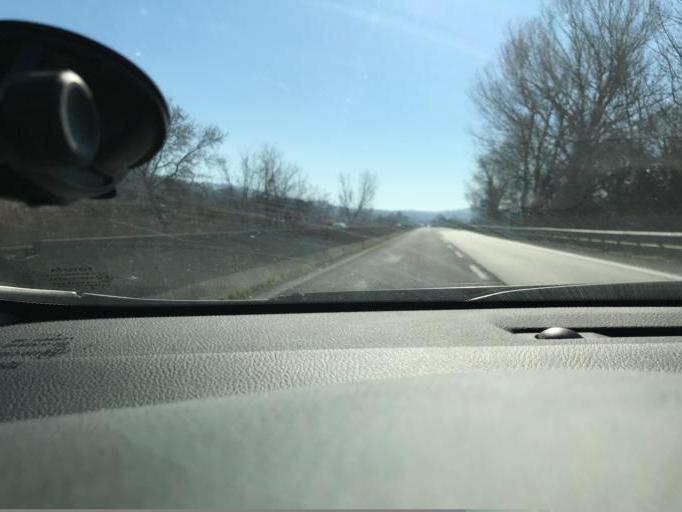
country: IT
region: Umbria
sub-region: Provincia di Perugia
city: Torgiano
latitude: 43.0106
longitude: 12.4259
